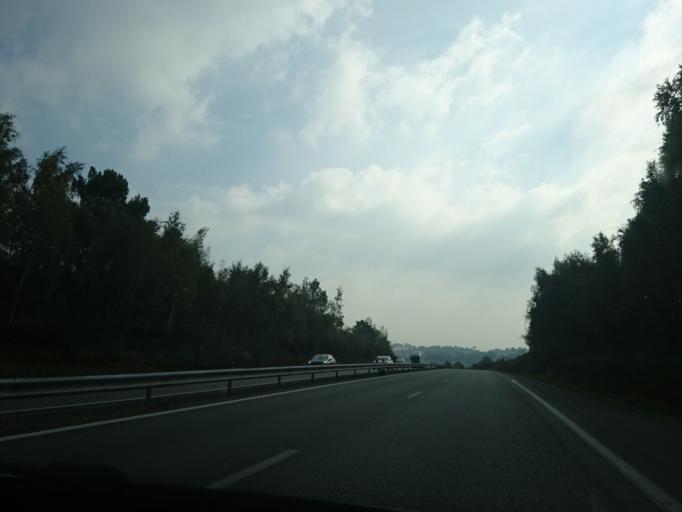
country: FR
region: Brittany
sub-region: Departement d'Ille-et-Vilaine
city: Bain-de-Bretagne
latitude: 47.8430
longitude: -1.6963
